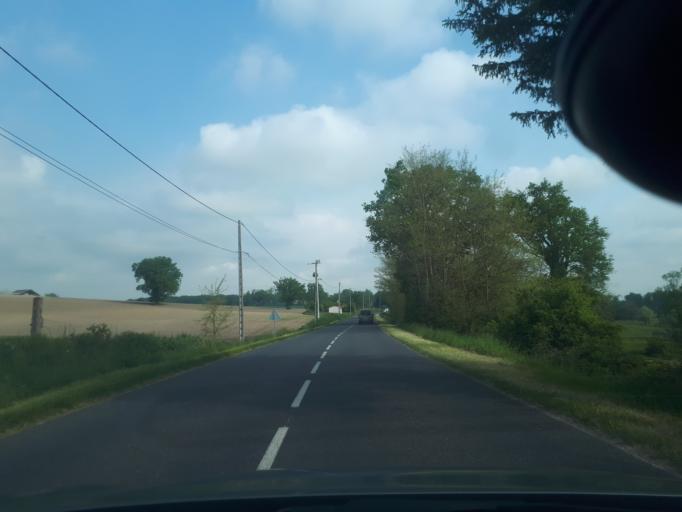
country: FR
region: Auvergne
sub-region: Departement de l'Allier
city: Lapalisse
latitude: 46.3385
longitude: 3.5805
